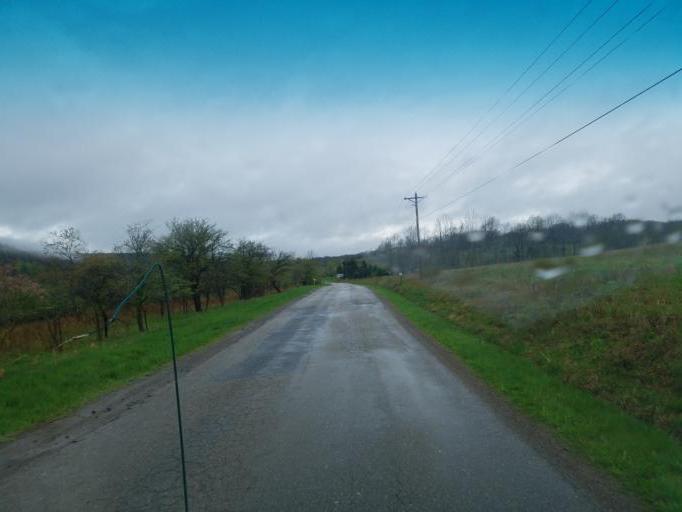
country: US
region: Pennsylvania
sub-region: Tioga County
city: Westfield
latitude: 41.9766
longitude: -77.6750
